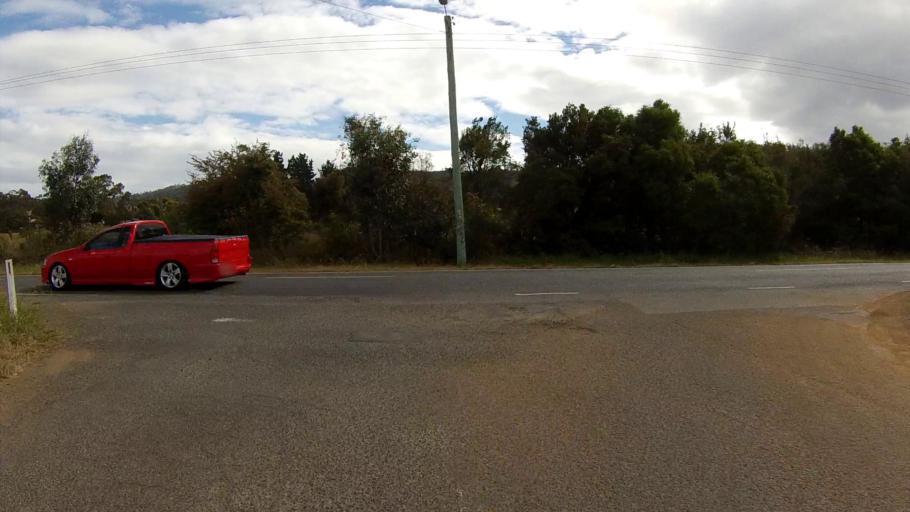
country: AU
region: Tasmania
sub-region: Clarence
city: Acton Park
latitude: -42.8663
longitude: 147.4828
